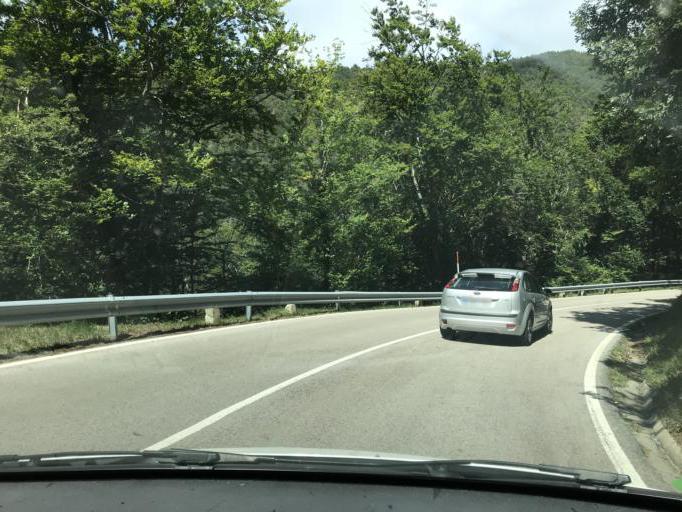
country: ES
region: Cantabria
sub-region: Provincia de Cantabria
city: Cabezon de Liebana
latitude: 43.0757
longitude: -4.4751
